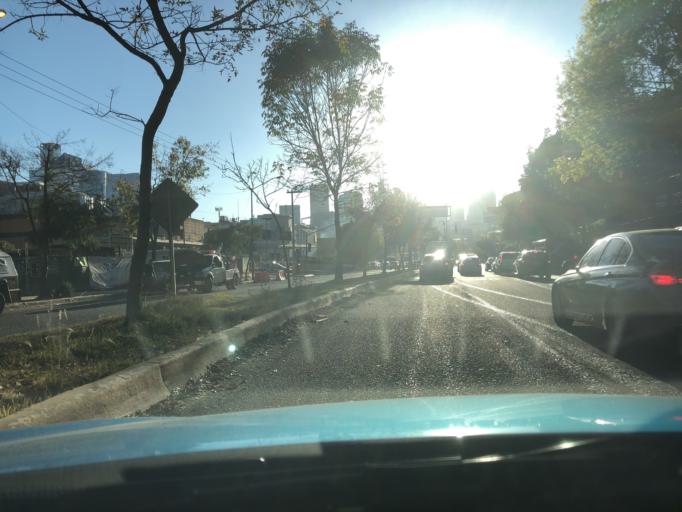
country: MX
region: Mexico City
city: Col. Bosques de las Lomas
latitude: 19.3648
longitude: -99.2699
